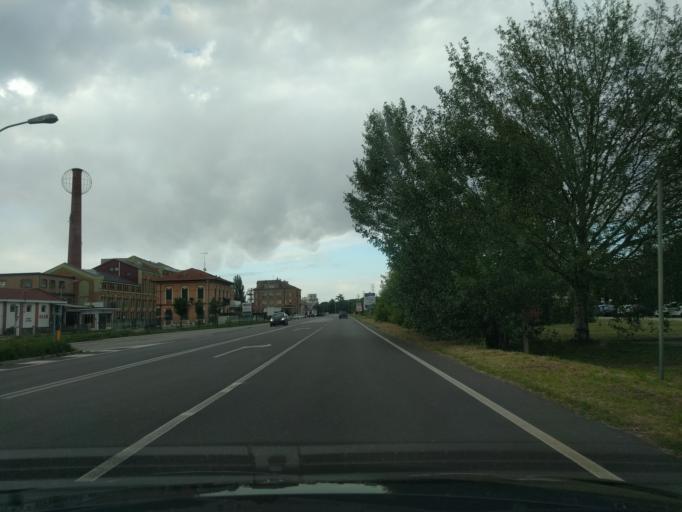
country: IT
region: Veneto
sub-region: Provincia di Rovigo
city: Santa Maria Maddalena
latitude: 44.8790
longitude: 11.6065
